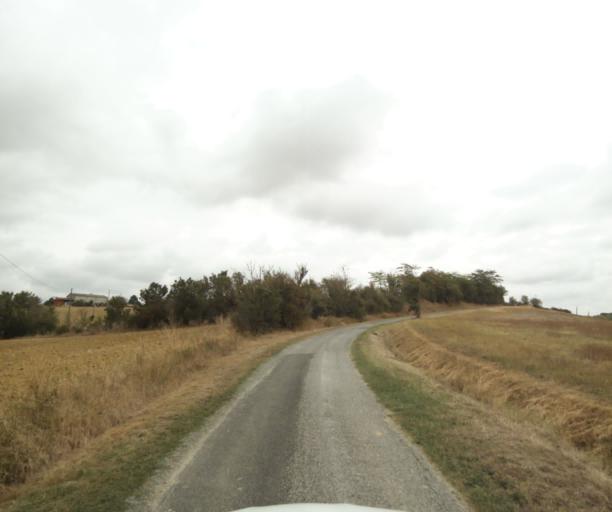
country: FR
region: Midi-Pyrenees
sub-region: Departement de la Haute-Garonne
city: Villefranche-de-Lauragais
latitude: 43.4179
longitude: 1.7333
